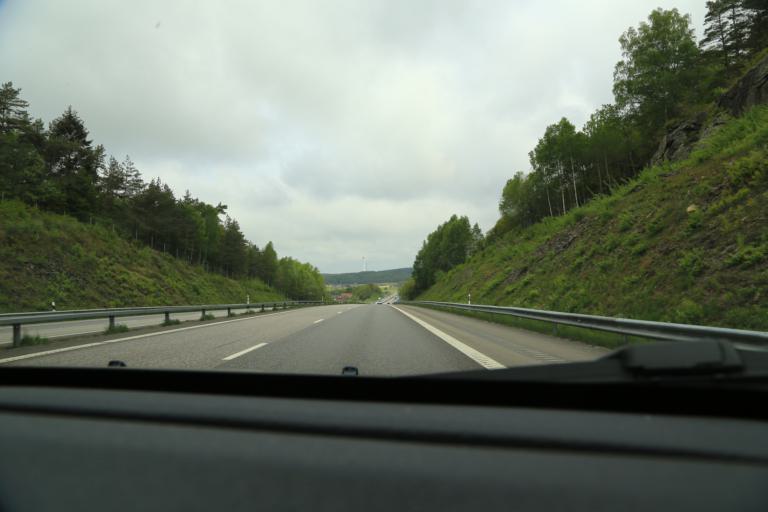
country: SE
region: Halland
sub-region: Kungsbacka Kommun
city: Frillesas
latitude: 57.3126
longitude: 12.2119
